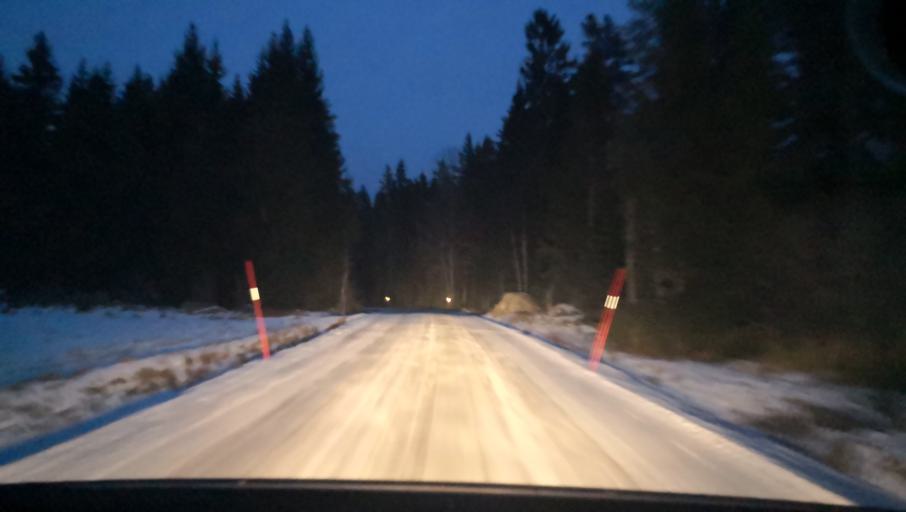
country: SE
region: Uppsala
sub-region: Heby Kommun
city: Tarnsjo
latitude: 60.2467
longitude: 16.7251
